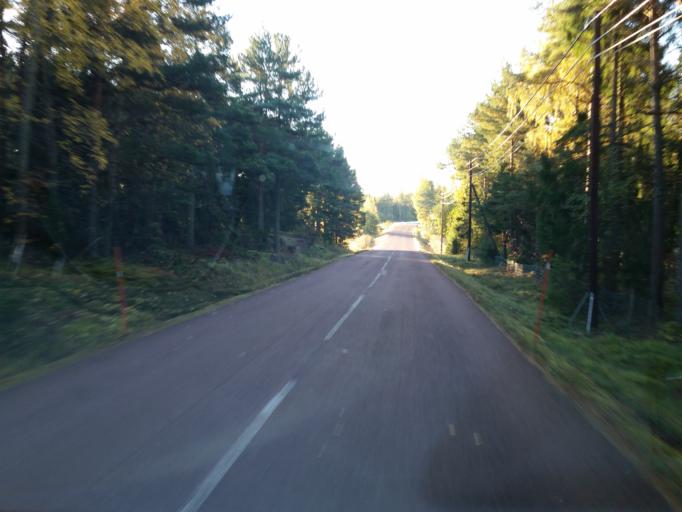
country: AX
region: Alands skaergard
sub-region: Vardoe
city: Vardoe
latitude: 60.2972
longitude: 20.3840
